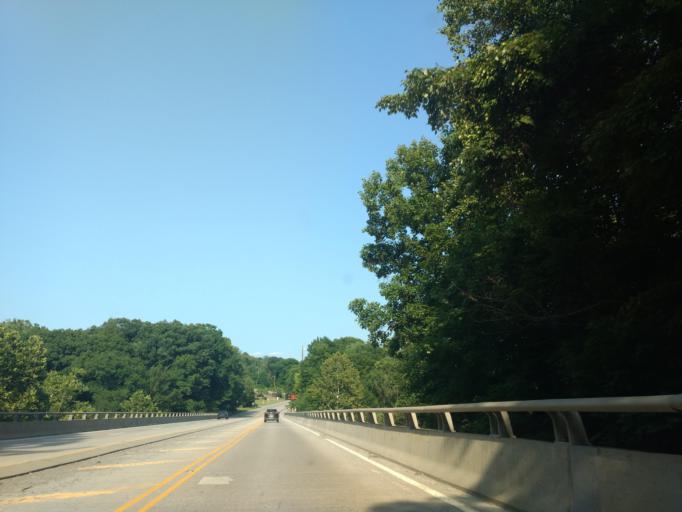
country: US
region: Pennsylvania
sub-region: Lawrence County
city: Ellport
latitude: 40.9694
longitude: -80.1819
